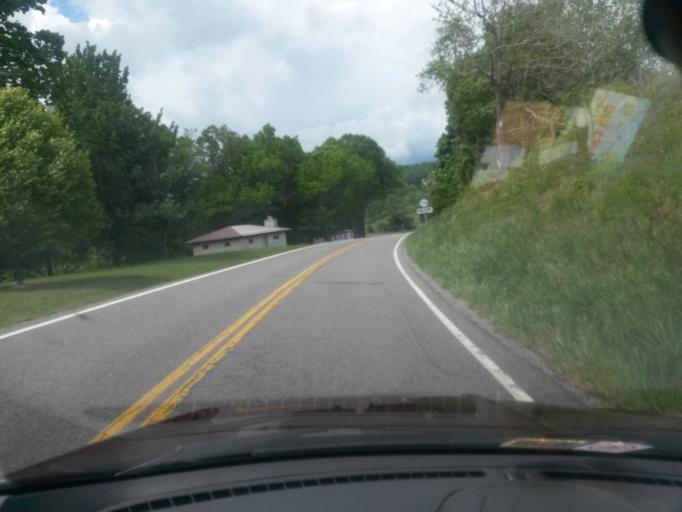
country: US
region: Virginia
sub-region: Floyd County
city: Floyd
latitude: 36.8581
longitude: -80.3226
